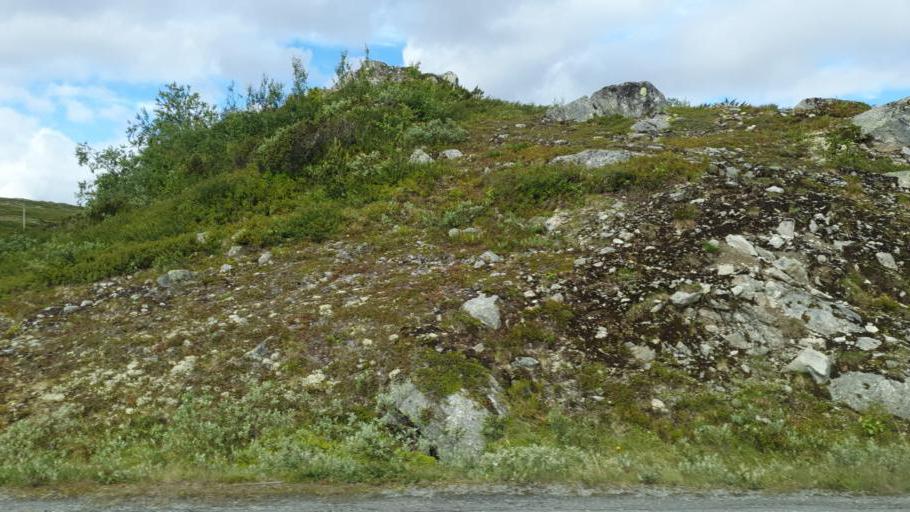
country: NO
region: Oppland
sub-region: Vestre Slidre
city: Slidre
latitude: 61.3245
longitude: 8.8044
